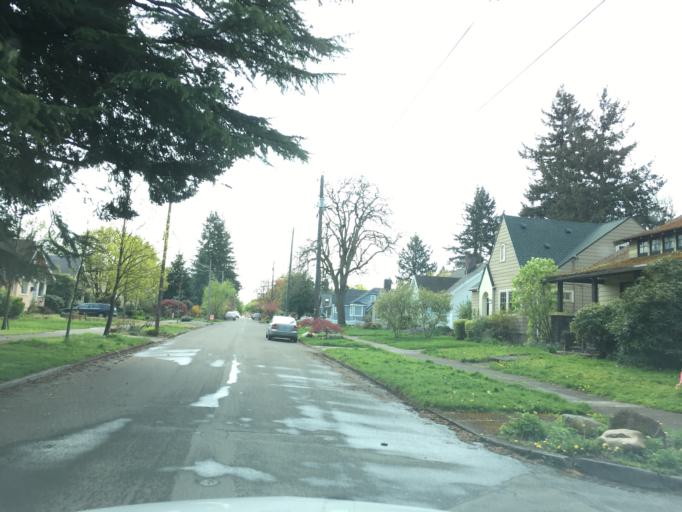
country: US
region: Oregon
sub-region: Multnomah County
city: Lents
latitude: 45.5504
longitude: -122.5984
